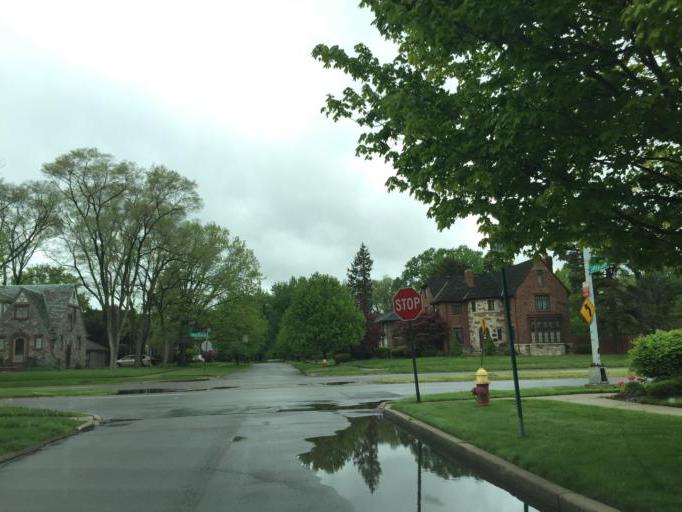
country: US
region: Michigan
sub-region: Oakland County
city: Southfield
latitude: 42.4071
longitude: -83.2316
